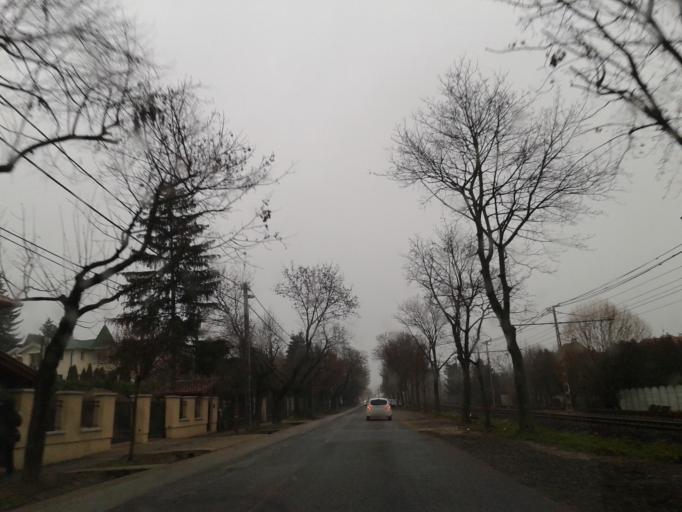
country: HU
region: Budapest
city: Budapest XXII. keruelet
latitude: 47.4426
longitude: 19.0166
